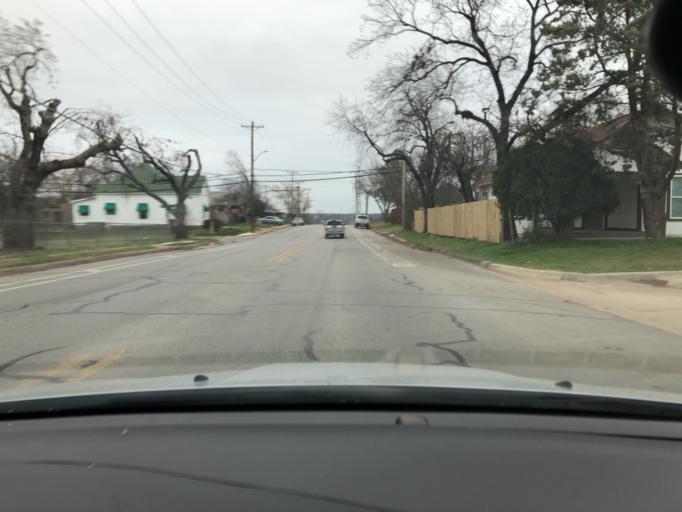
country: US
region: Texas
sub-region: Tarrant County
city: Fort Worth
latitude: 32.7268
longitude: -97.3027
